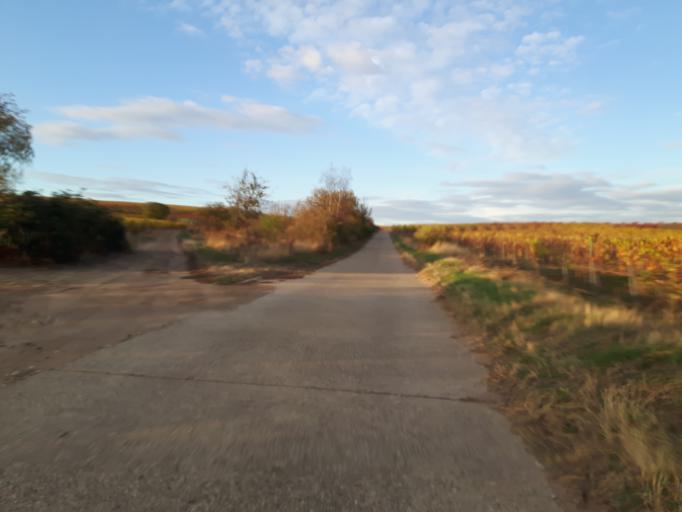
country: DE
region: Rheinland-Pfalz
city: Bockenheim
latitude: 49.6245
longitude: 8.1802
